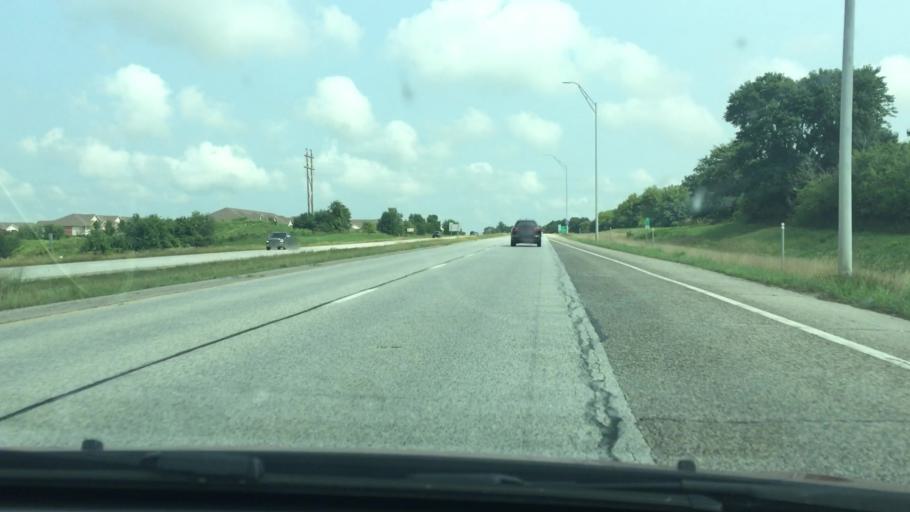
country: US
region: Iowa
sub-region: Scott County
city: Bettendorf
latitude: 41.5801
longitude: -90.5219
